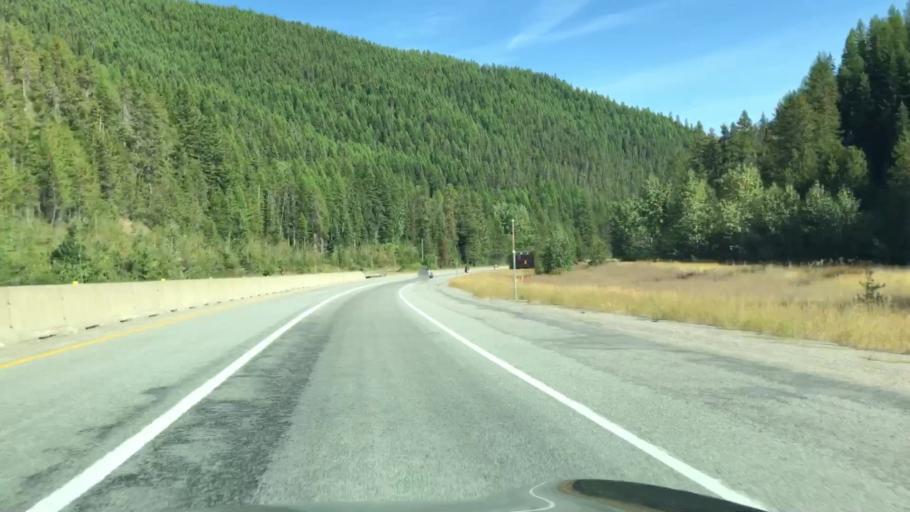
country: US
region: Idaho
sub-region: Shoshone County
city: Wallace
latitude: 47.4312
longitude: -115.6454
